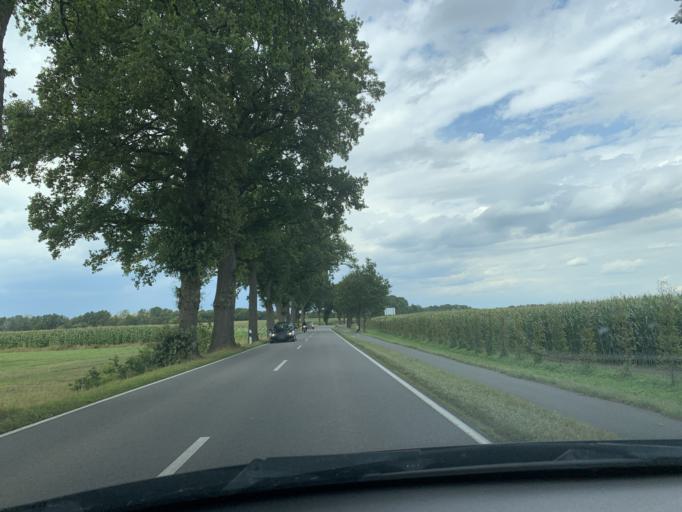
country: DE
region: Lower Saxony
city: Westerstede
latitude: 53.2289
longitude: 7.9021
